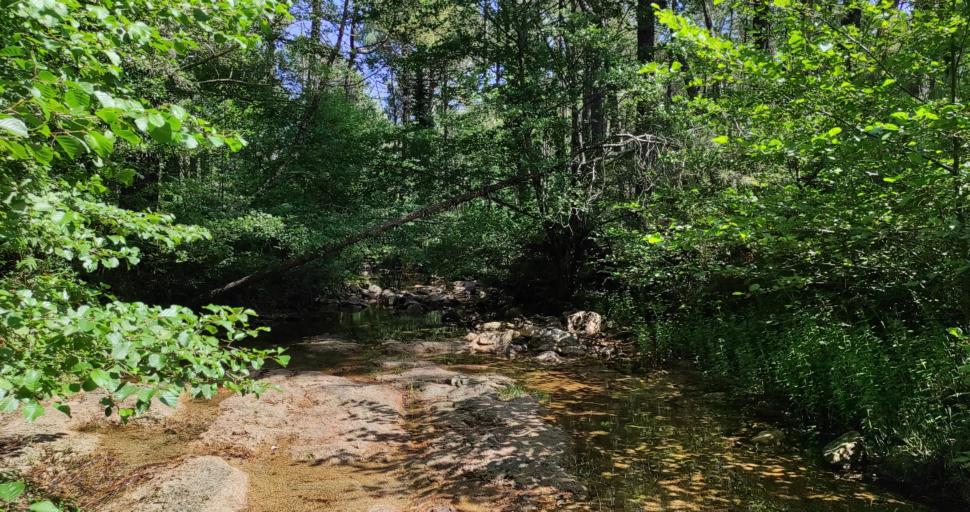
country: FR
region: Corsica
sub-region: Departement de la Corse-du-Sud
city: Zonza
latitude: 41.6815
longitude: 9.2095
